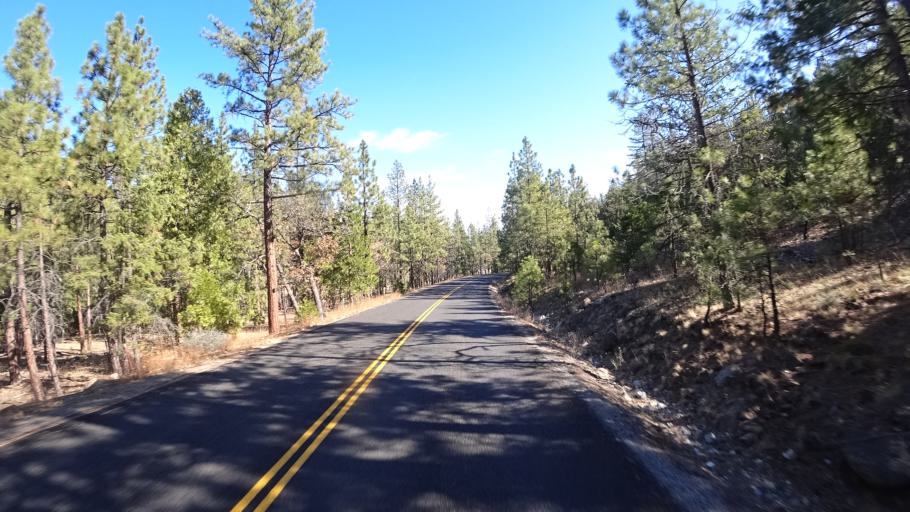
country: US
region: California
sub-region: Siskiyou County
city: Weed
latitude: 41.4328
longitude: -122.4936
